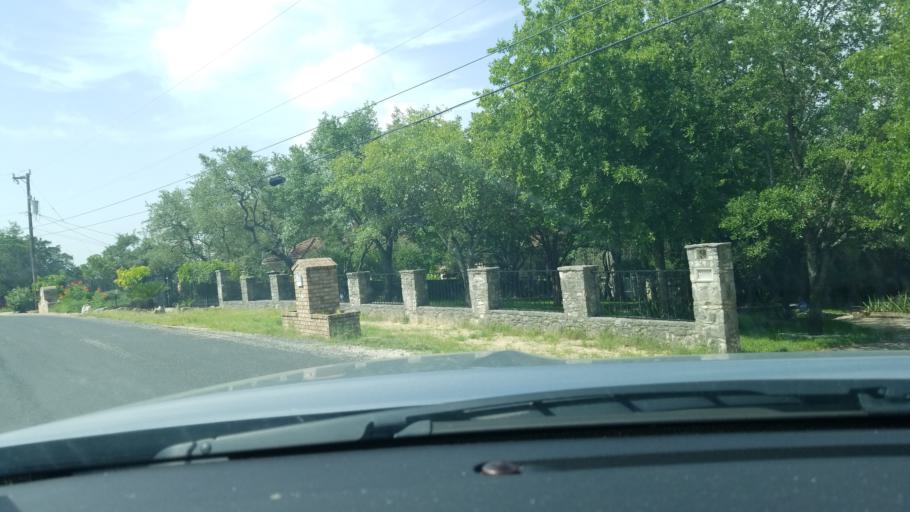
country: US
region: Texas
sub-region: Bexar County
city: Timberwood Park
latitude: 29.6866
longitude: -98.4932
